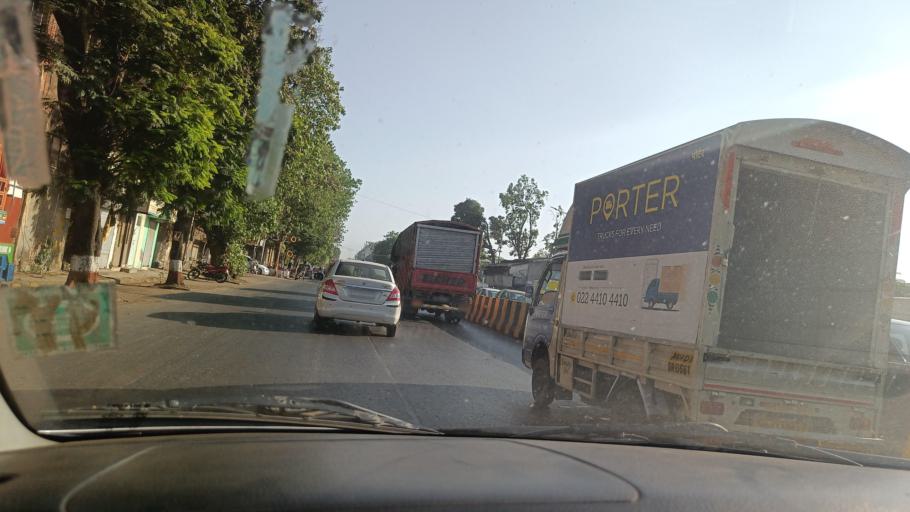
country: IN
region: Maharashtra
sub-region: Mumbai Suburban
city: Mumbai
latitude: 18.9556
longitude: 72.8423
